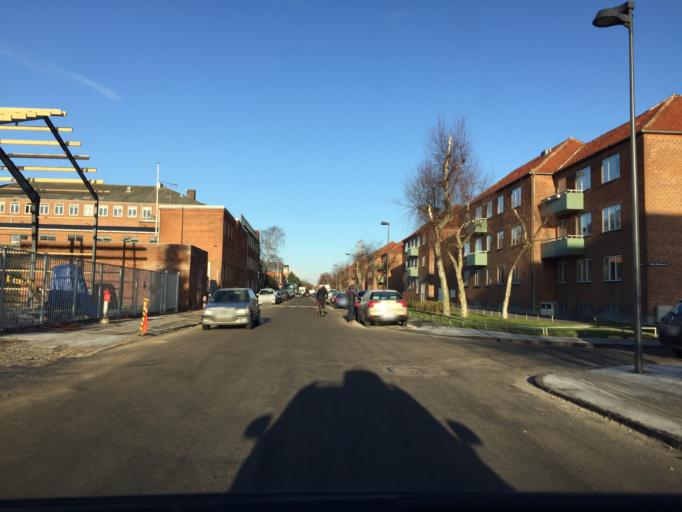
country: DK
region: Capital Region
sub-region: Kobenhavn
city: Vanlose
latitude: 55.6581
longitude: 12.5055
